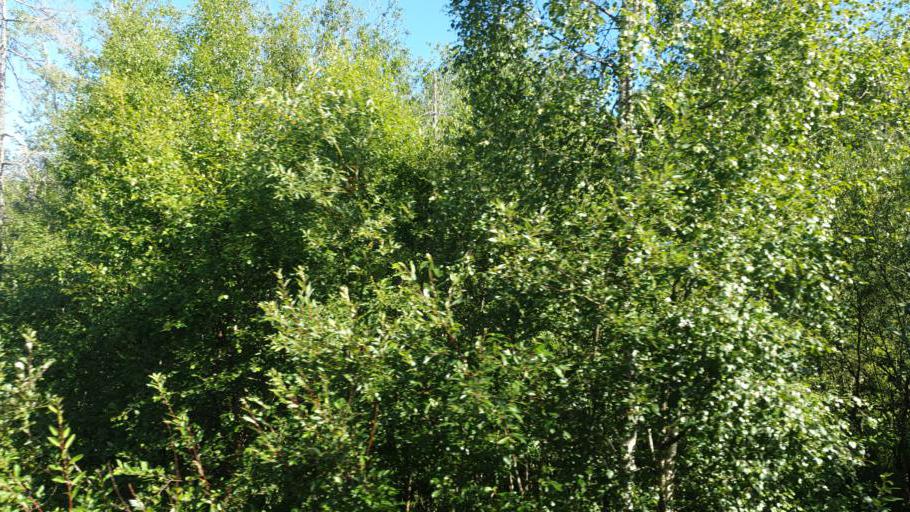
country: NO
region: Sor-Trondelag
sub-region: Orkdal
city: Orkanger
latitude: 63.1953
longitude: 9.7866
